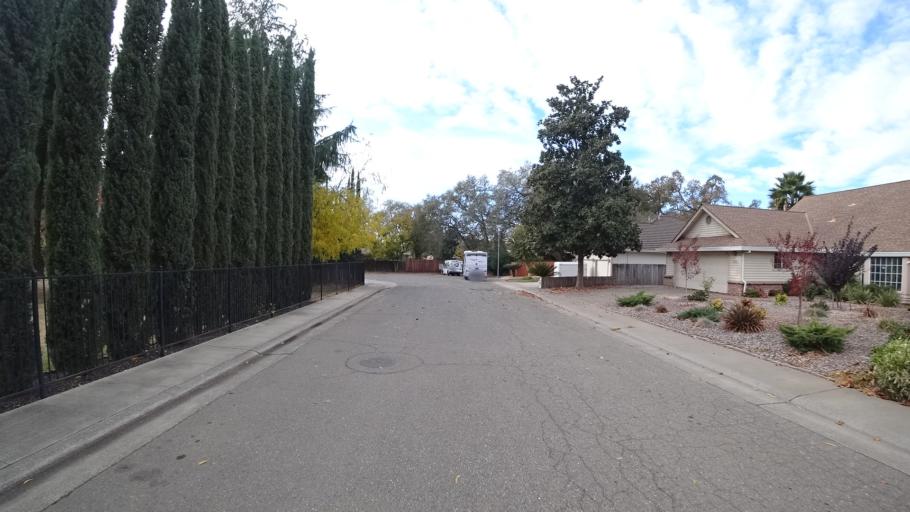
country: US
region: California
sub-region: Sacramento County
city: Citrus Heights
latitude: 38.7046
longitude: -121.2668
